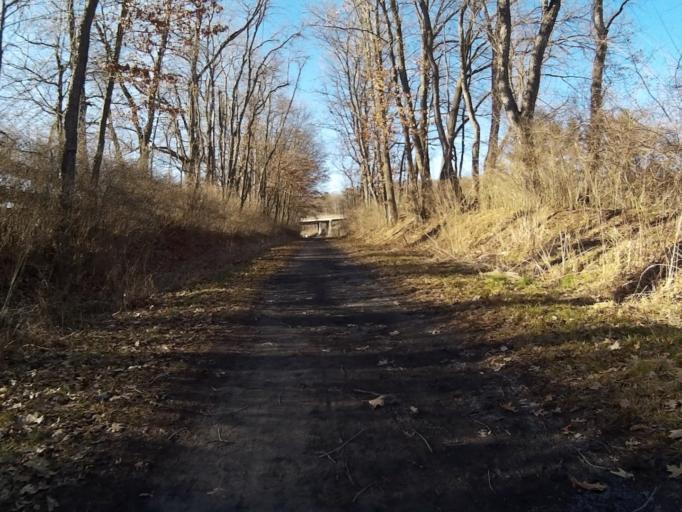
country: US
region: Pennsylvania
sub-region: Centre County
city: State College
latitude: 40.8182
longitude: -77.8789
